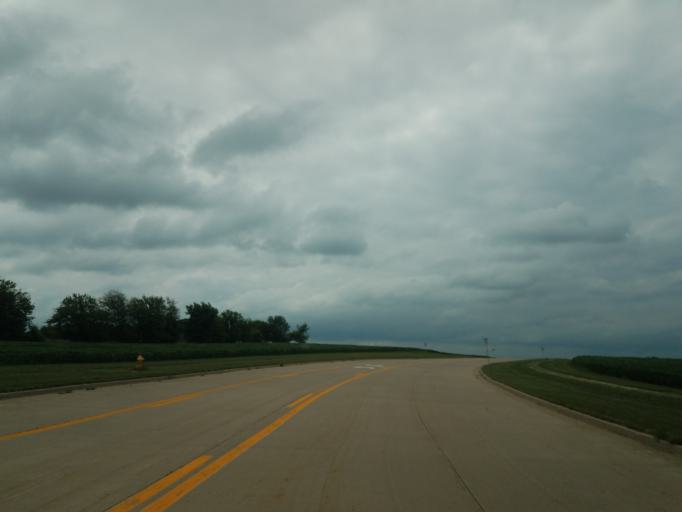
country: US
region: Illinois
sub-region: McLean County
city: Twin Grove
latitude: 40.4416
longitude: -89.0493
